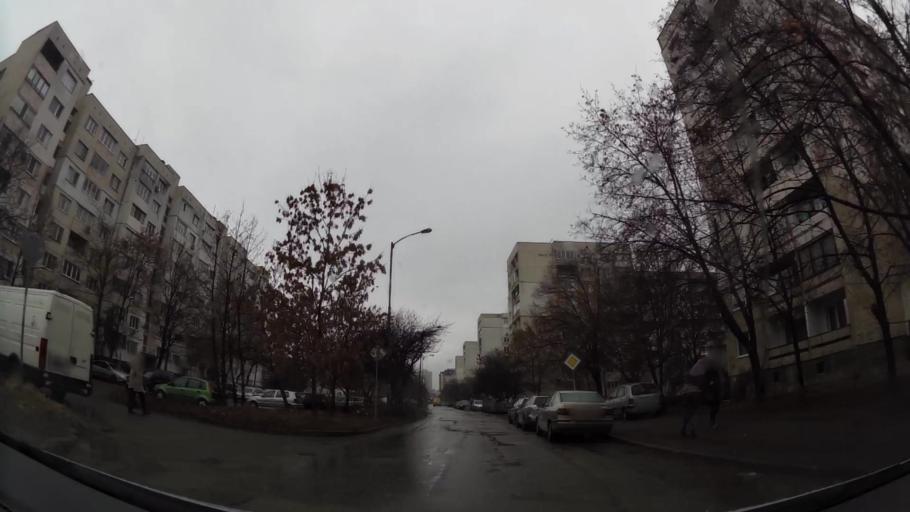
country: BG
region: Sofia-Capital
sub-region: Stolichna Obshtina
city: Sofia
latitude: 42.6375
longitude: 23.3800
